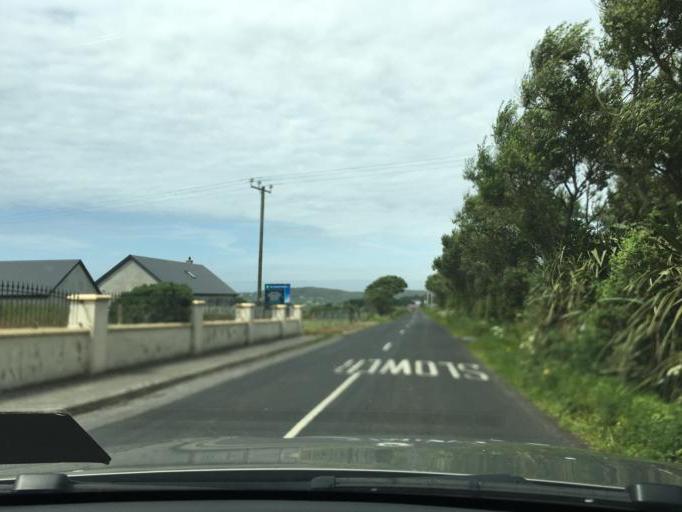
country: IE
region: Ulster
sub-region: County Donegal
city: Carndonagh
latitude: 55.3501
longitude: -7.3155
